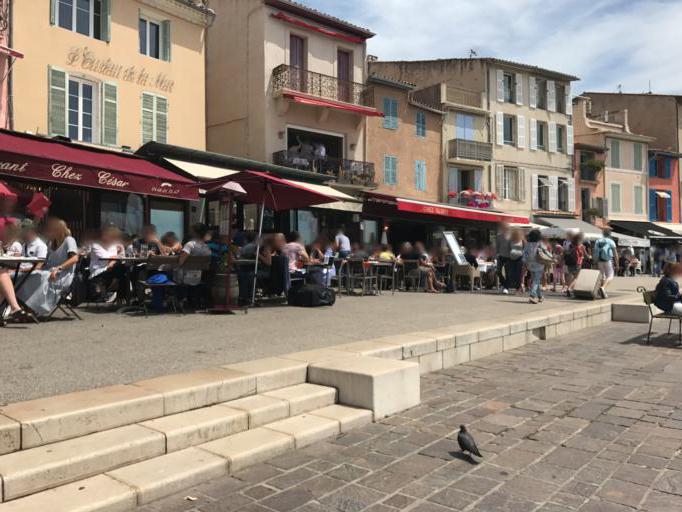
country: FR
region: Provence-Alpes-Cote d'Azur
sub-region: Departement des Bouches-du-Rhone
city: Cassis
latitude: 43.2148
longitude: 5.5371
